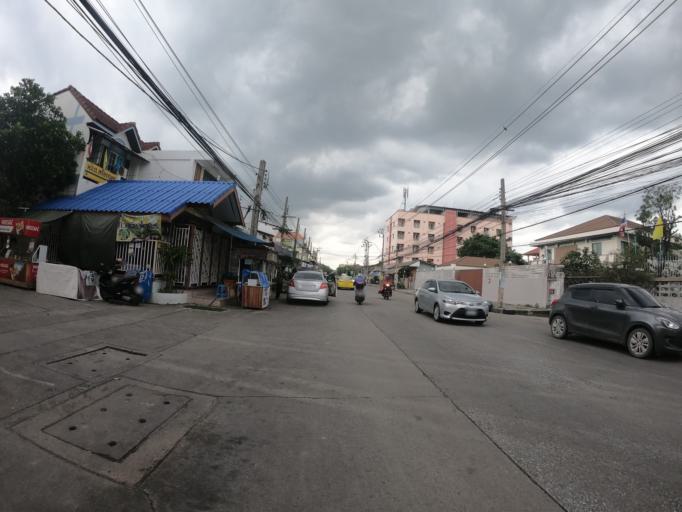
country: TH
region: Bangkok
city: Suan Luang
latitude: 13.7123
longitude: 100.6593
